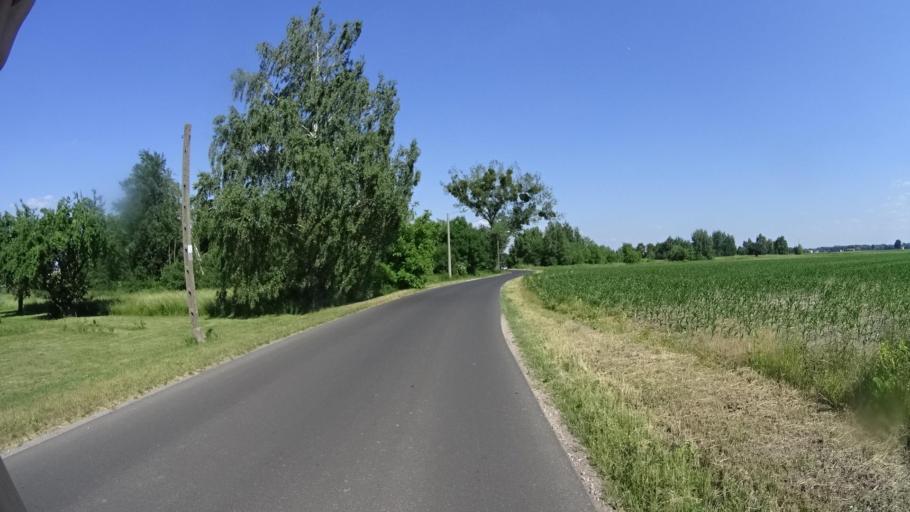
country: PL
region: Masovian Voivodeship
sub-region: Powiat warszawski zachodni
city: Blonie
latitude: 52.1633
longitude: 20.6462
